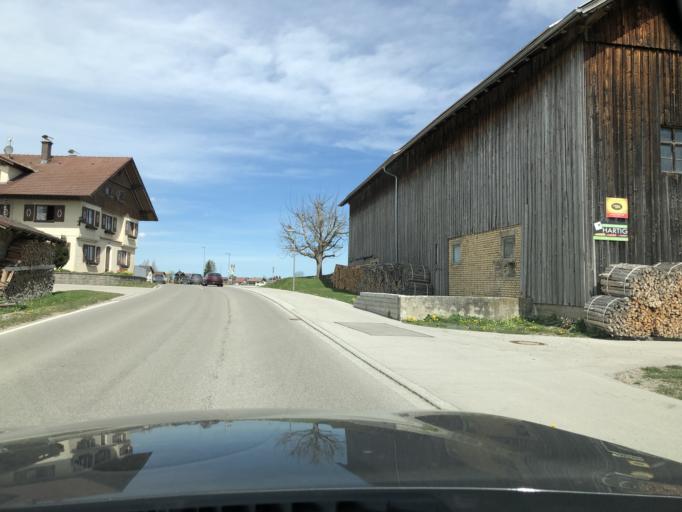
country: DE
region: Bavaria
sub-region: Swabia
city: Lengenwang
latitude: 47.6942
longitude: 10.6072
